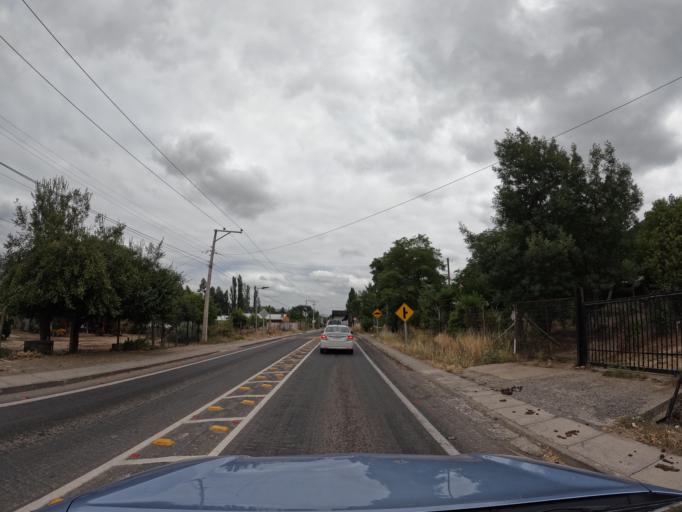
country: CL
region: Maule
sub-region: Provincia de Curico
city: Teno
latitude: -34.8046
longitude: -71.2209
